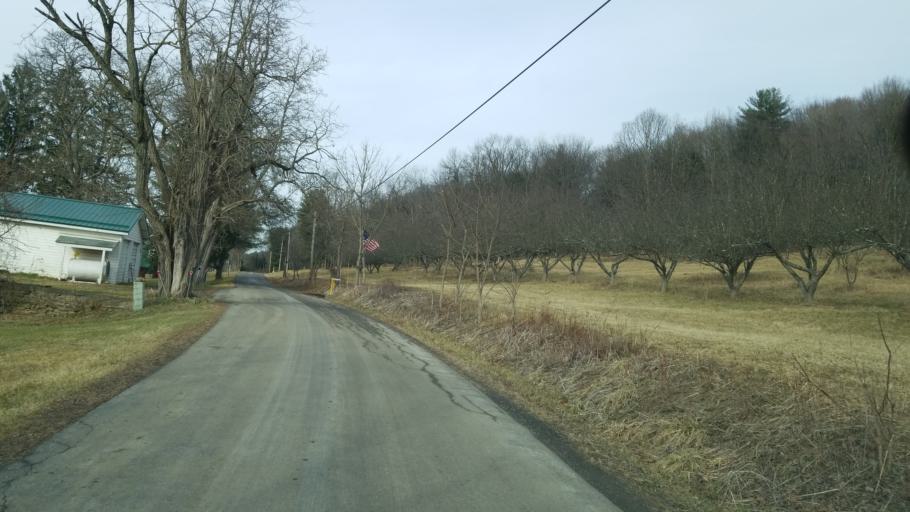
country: US
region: Pennsylvania
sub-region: Jefferson County
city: Punxsutawney
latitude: 40.8309
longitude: -78.9869
